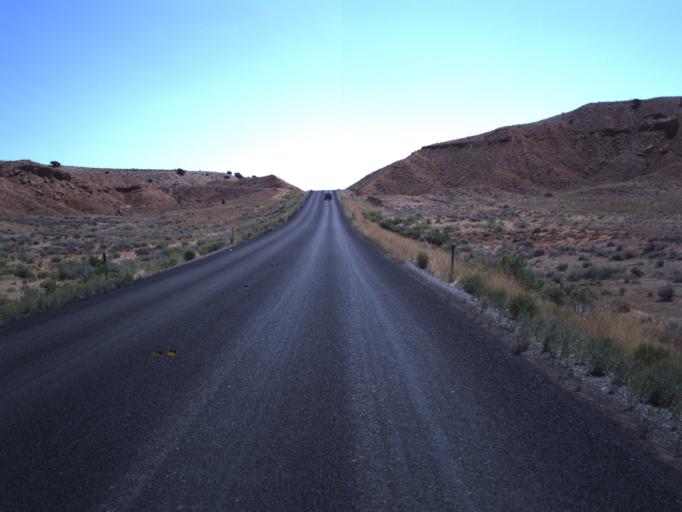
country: US
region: Utah
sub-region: Uintah County
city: Maeser
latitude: 40.4107
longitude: -109.7167
